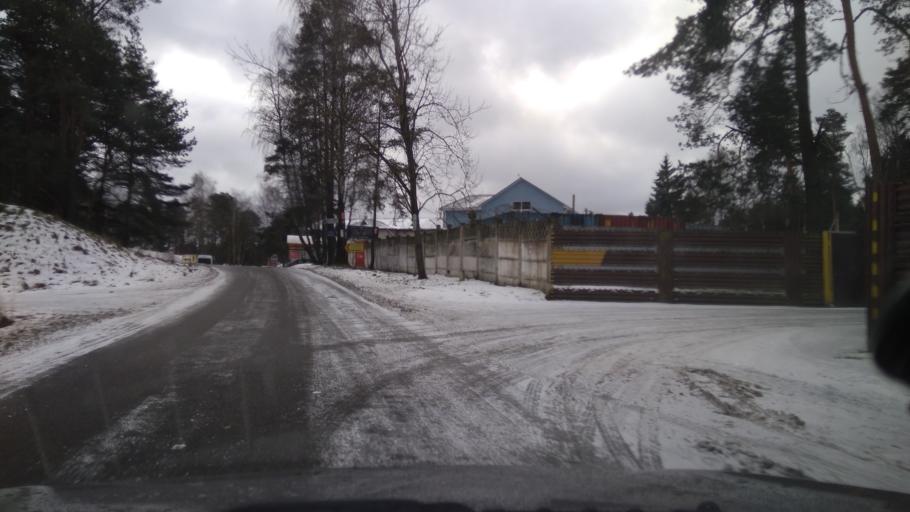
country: BY
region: Minsk
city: Borovlyany
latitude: 53.9625
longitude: 27.6480
